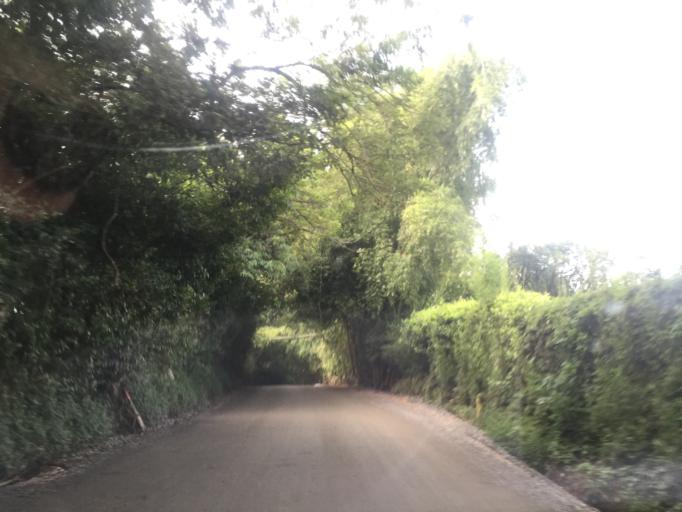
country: CO
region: Quindio
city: La Tebaida
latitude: 4.4622
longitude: -75.8039
